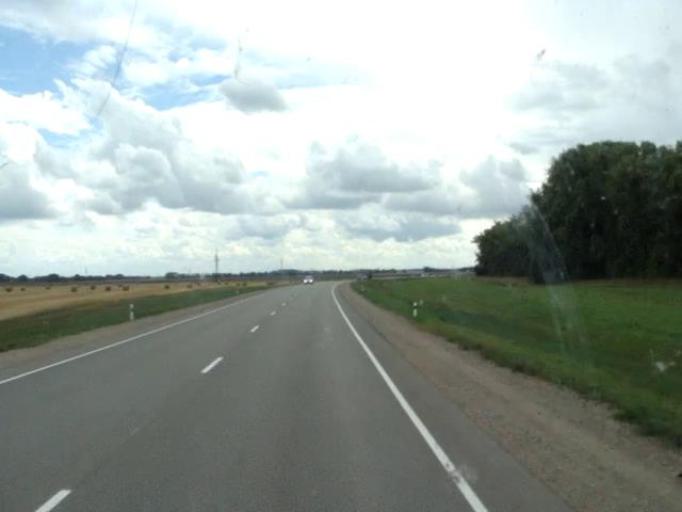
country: RU
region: Altai Krai
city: Shubenka
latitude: 52.6813
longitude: 85.0474
